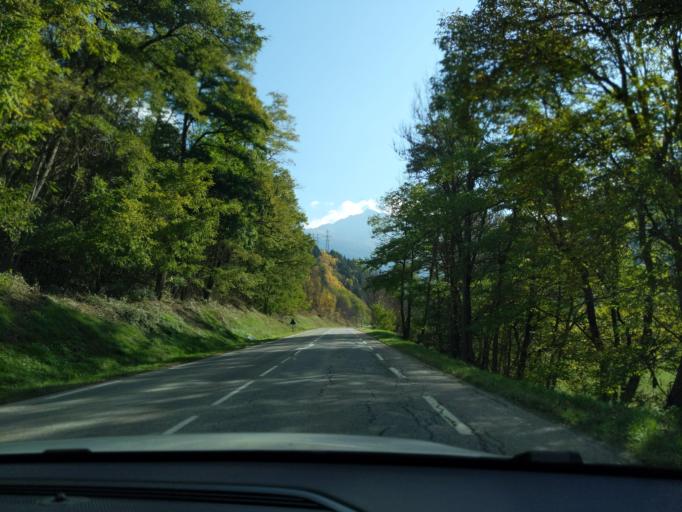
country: FR
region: Rhone-Alpes
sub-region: Departement de la Savoie
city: Seez
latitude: 45.6127
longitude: 6.8291
